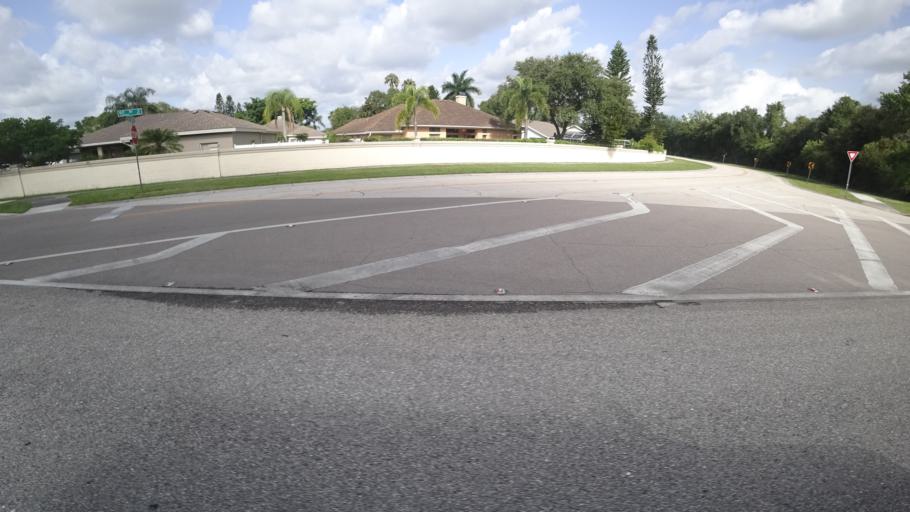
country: US
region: Florida
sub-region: Manatee County
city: Samoset
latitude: 27.4437
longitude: -82.4810
